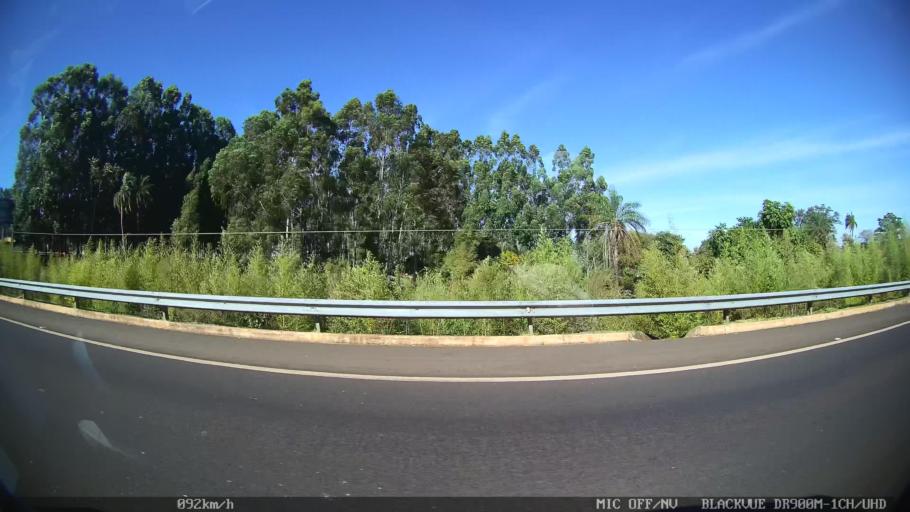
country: BR
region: Sao Paulo
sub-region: Franca
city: Franca
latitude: -20.5766
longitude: -47.3548
